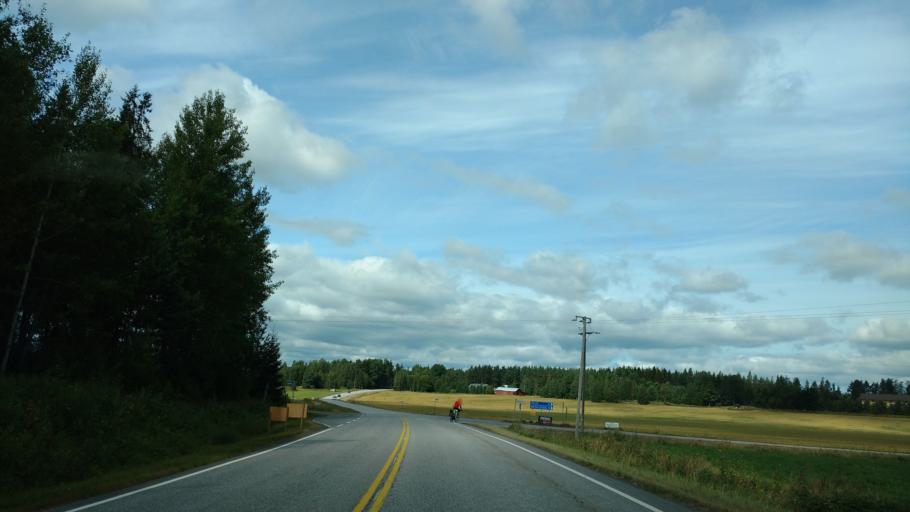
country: FI
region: Varsinais-Suomi
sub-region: Salo
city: Saerkisalo
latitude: 60.1735
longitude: 22.9665
